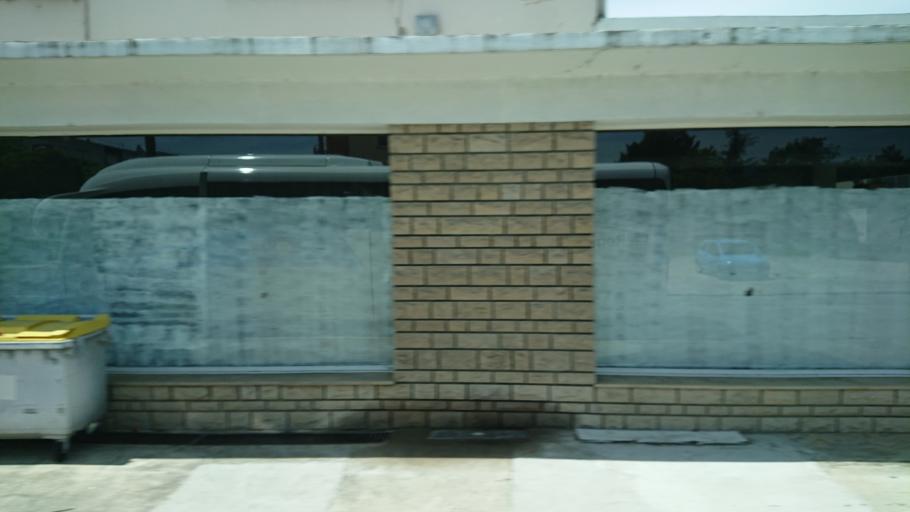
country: FR
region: Rhone-Alpes
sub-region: Departement de l'Ain
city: Saint-Denis-en-Bugey
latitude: 45.9565
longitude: 5.3327
